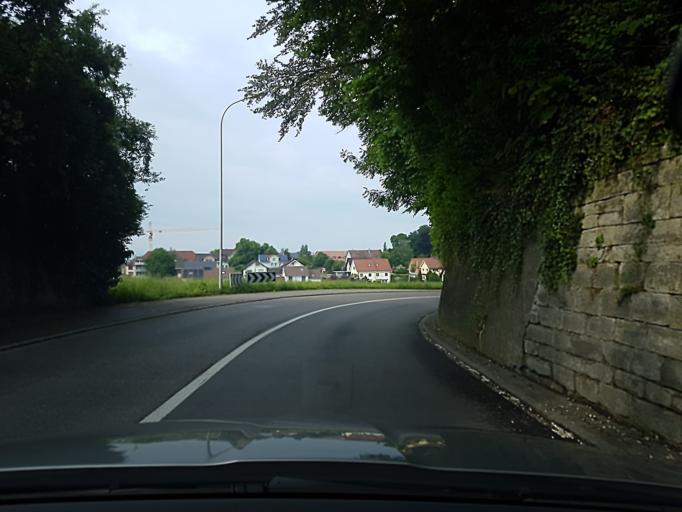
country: CH
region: Thurgau
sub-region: Arbon District
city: Egnach
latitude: 47.5272
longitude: 9.3661
